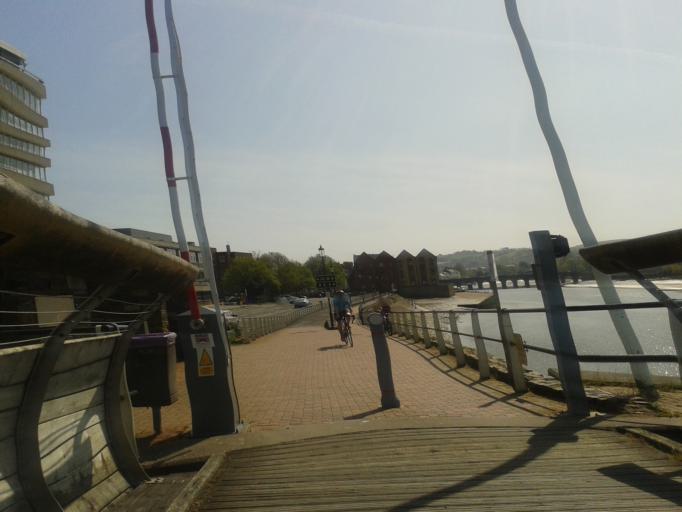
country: GB
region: England
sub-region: Devon
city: Barnstaple
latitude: 51.0812
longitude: -4.0668
